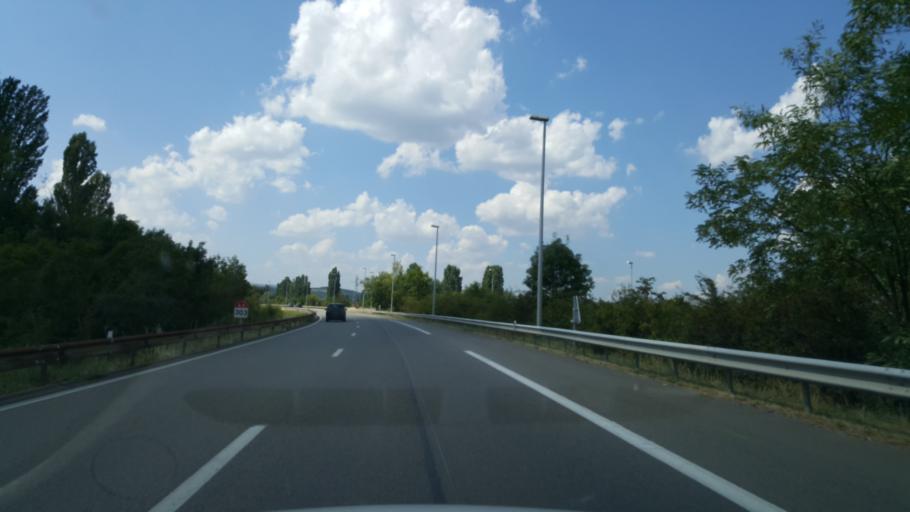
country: FR
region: Bourgogne
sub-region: Departement de la Cote-d'Or
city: Beaune
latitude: 47.0318
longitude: 4.8719
